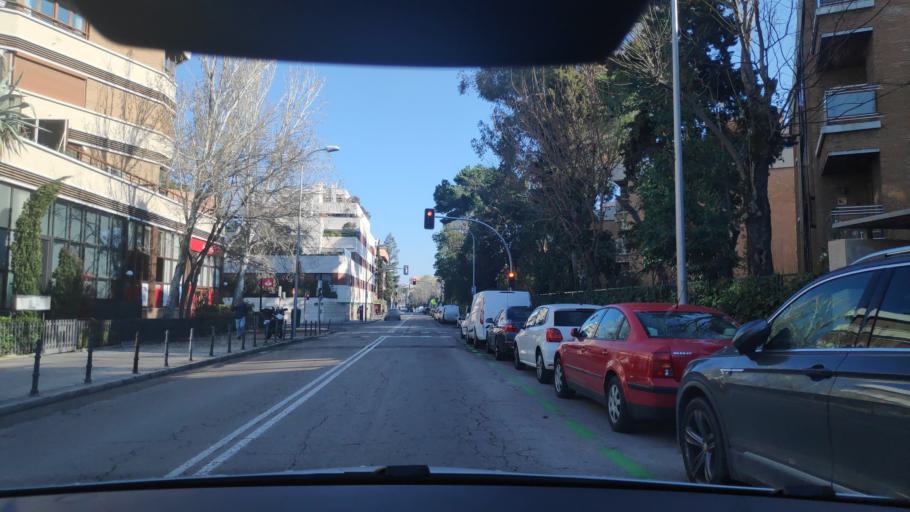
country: ES
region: Madrid
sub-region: Provincia de Madrid
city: Chamartin
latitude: 40.4633
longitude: -3.6800
